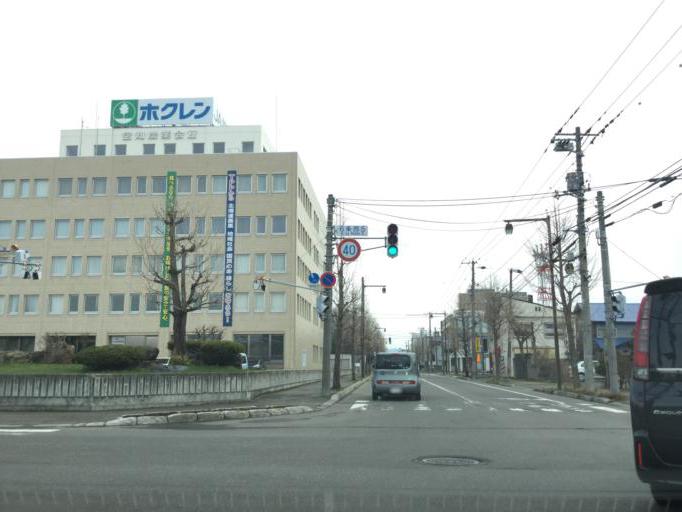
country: JP
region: Hokkaido
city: Iwamizawa
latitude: 43.1997
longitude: 141.7633
